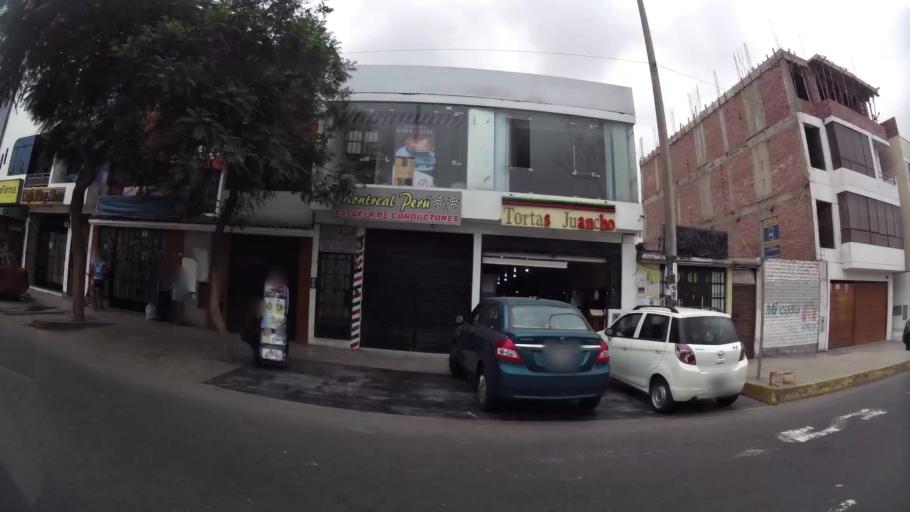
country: PE
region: Lima
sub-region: Lima
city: Surco
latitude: -12.1636
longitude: -76.9907
